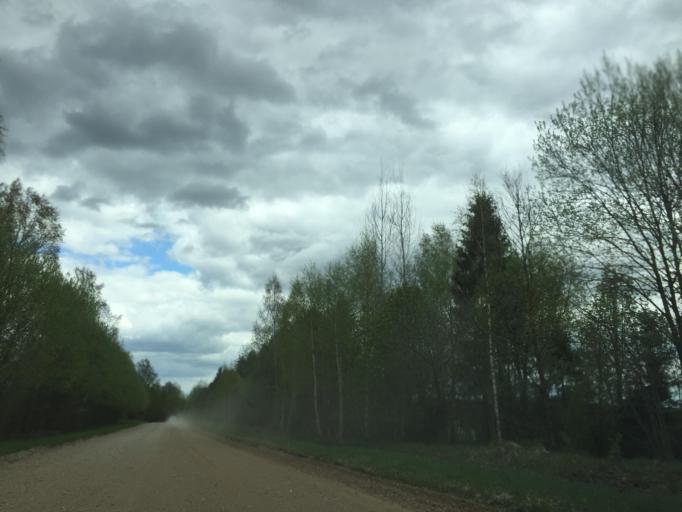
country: LV
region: Madonas Rajons
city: Madona
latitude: 56.9238
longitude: 26.0426
